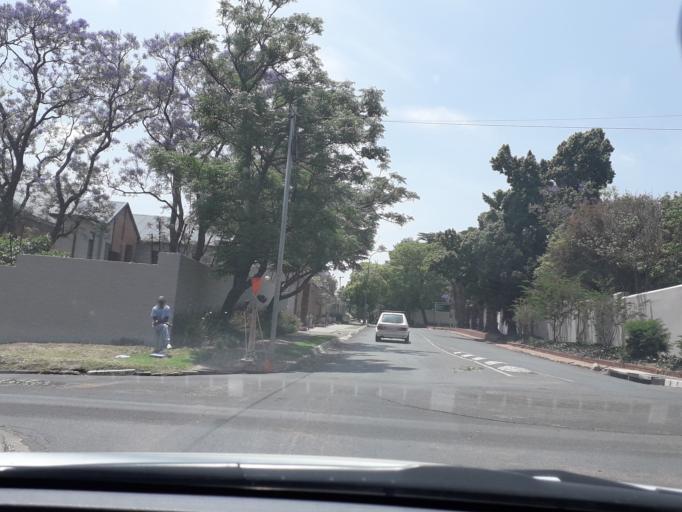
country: ZA
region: Gauteng
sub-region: City of Johannesburg Metropolitan Municipality
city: Johannesburg
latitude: -26.1085
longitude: 28.0256
